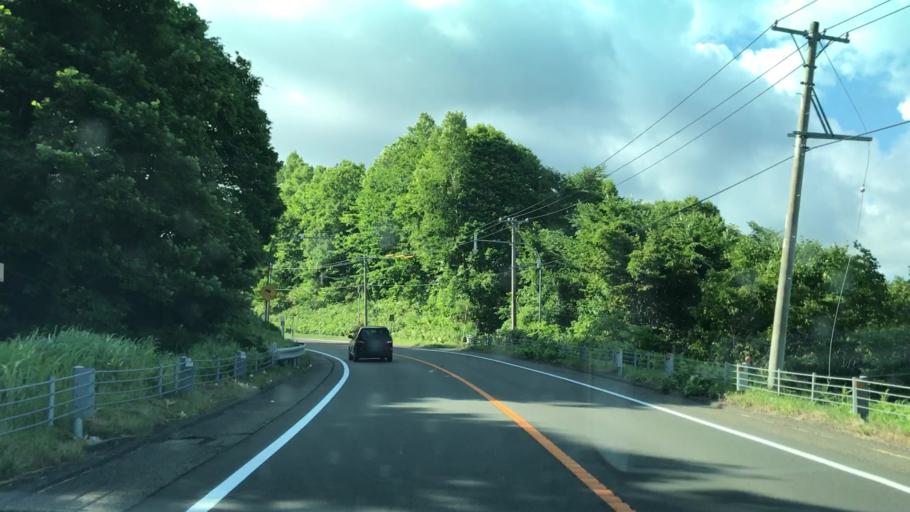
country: JP
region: Hokkaido
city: Shimo-furano
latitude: 42.9081
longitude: 142.4177
